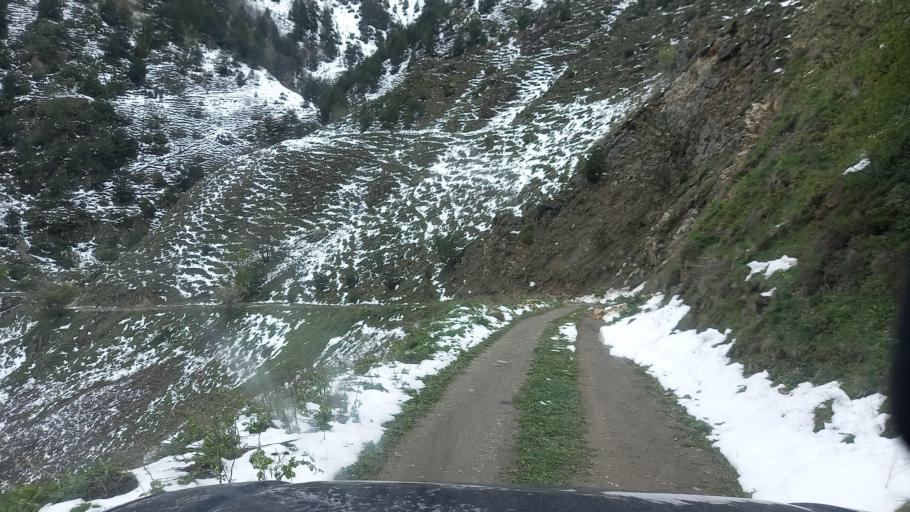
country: RU
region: North Ossetia
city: Mizur
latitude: 42.8028
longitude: 43.9351
